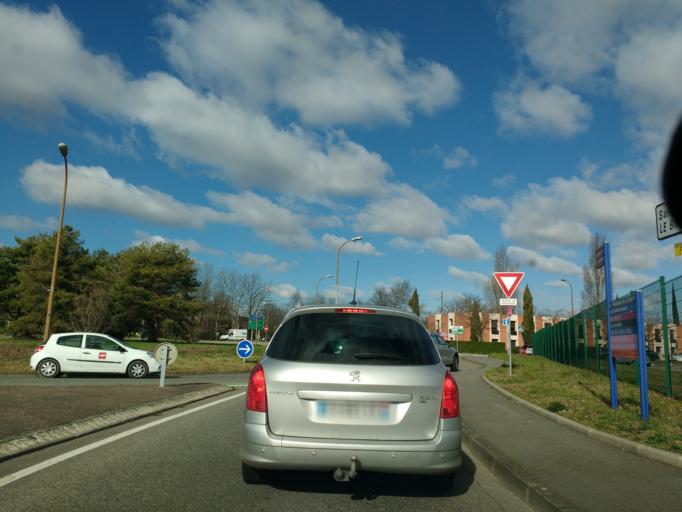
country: FR
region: Midi-Pyrenees
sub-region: Departement de la Haute-Garonne
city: Ramonville-Saint-Agne
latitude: 43.5537
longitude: 1.4846
